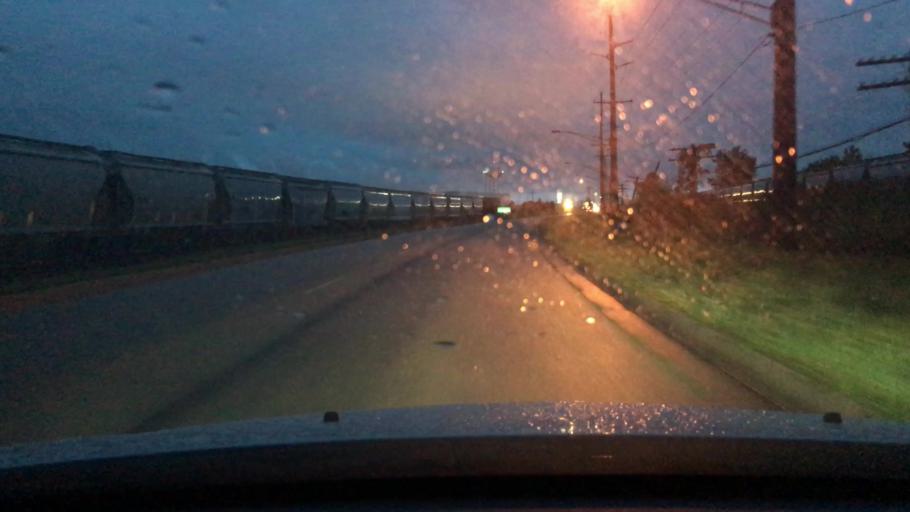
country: US
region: Illinois
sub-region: Ogle County
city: Rochelle
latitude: 41.9157
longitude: -89.0505
